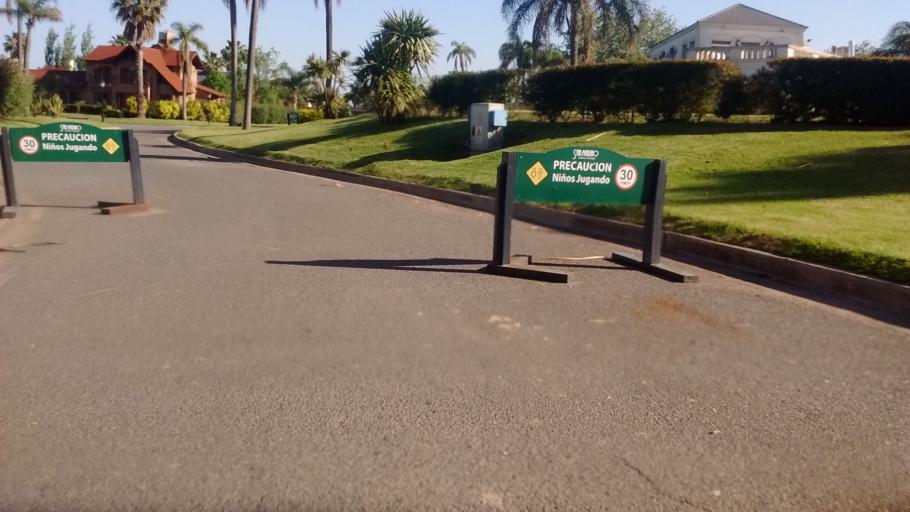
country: AR
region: Santa Fe
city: Funes
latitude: -32.9261
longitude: -60.8270
